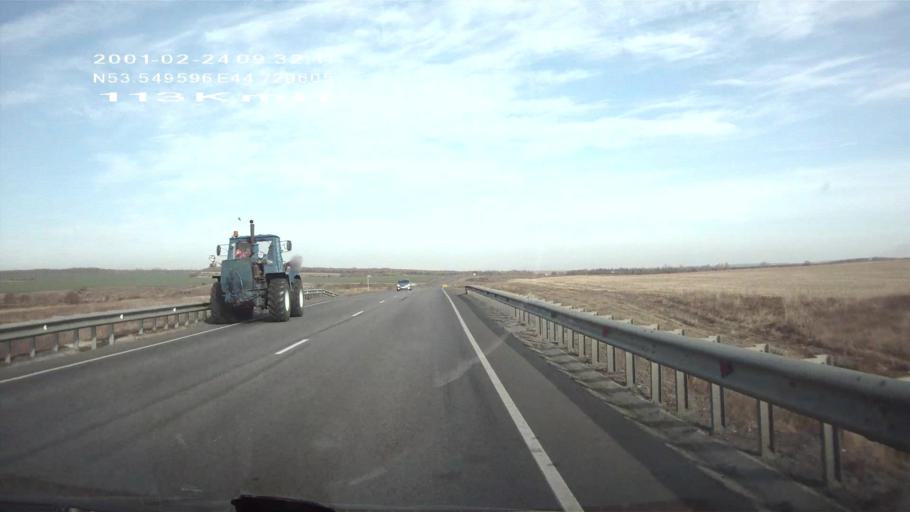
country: RU
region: Penza
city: Mokshan
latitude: 53.5497
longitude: 44.7296
